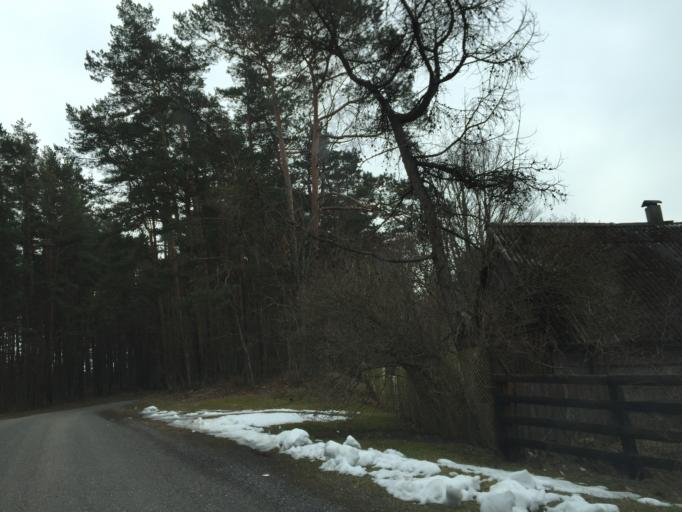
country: LV
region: Salacgrivas
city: Ainazi
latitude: 58.0344
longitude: 24.4623
